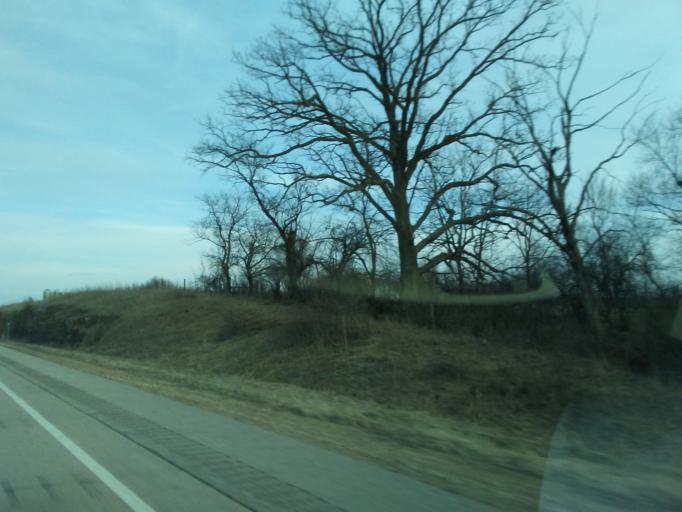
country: US
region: Wisconsin
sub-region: Iowa County
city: Barneveld
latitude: 43.0098
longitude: -89.8724
